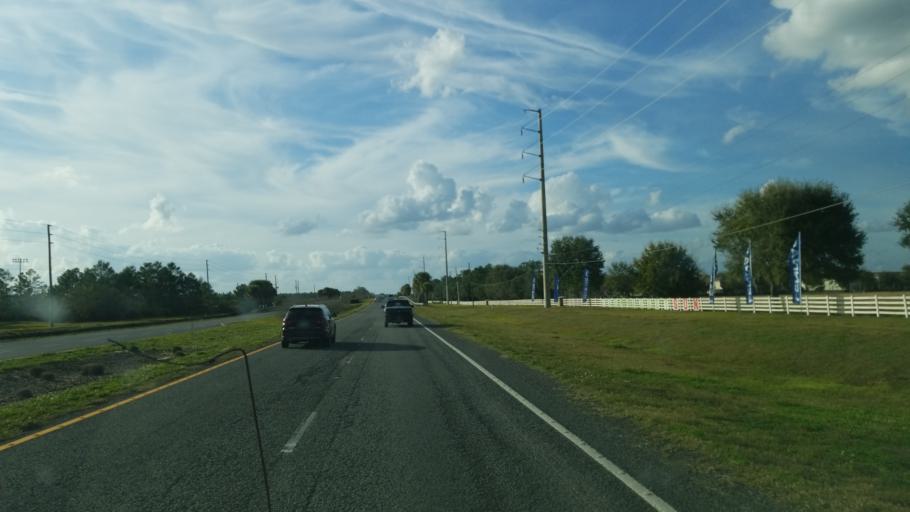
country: US
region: Florida
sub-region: Osceola County
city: Saint Cloud
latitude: 28.1882
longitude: -81.1472
